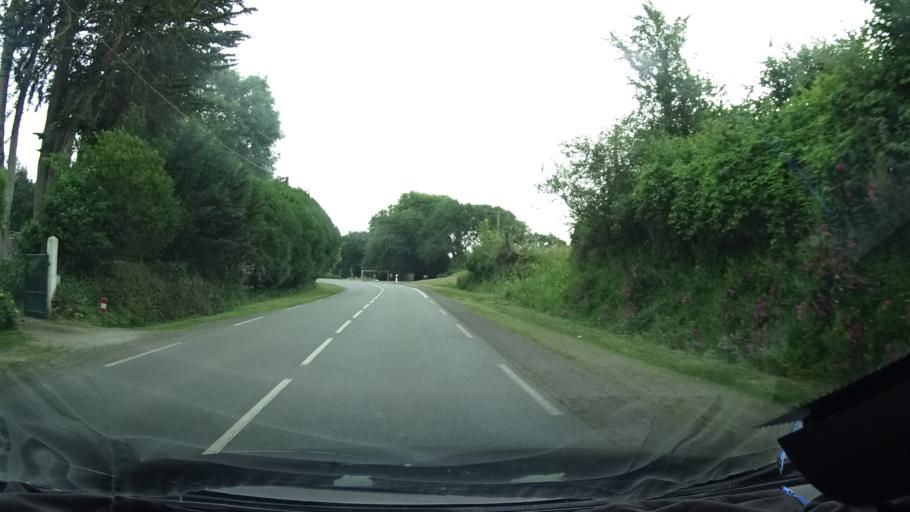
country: FR
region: Brittany
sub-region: Departement d'Ille-et-Vilaine
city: La Richardais
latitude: 48.6012
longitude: -2.0359
